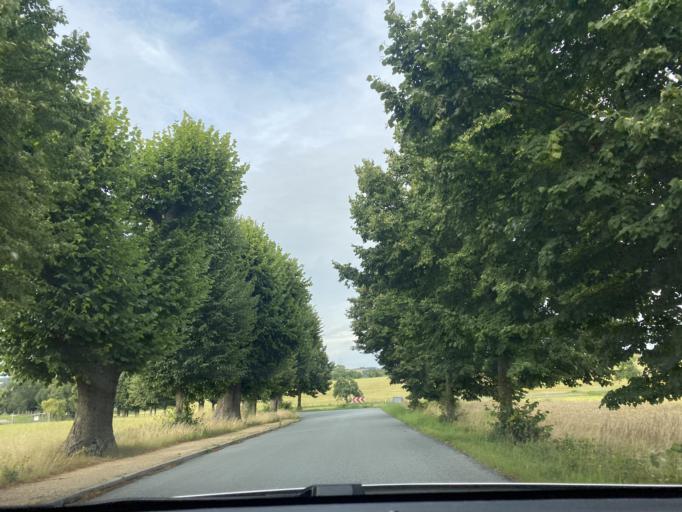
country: DE
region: Saxony
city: Herrnhut
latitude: 51.0222
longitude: 14.7582
